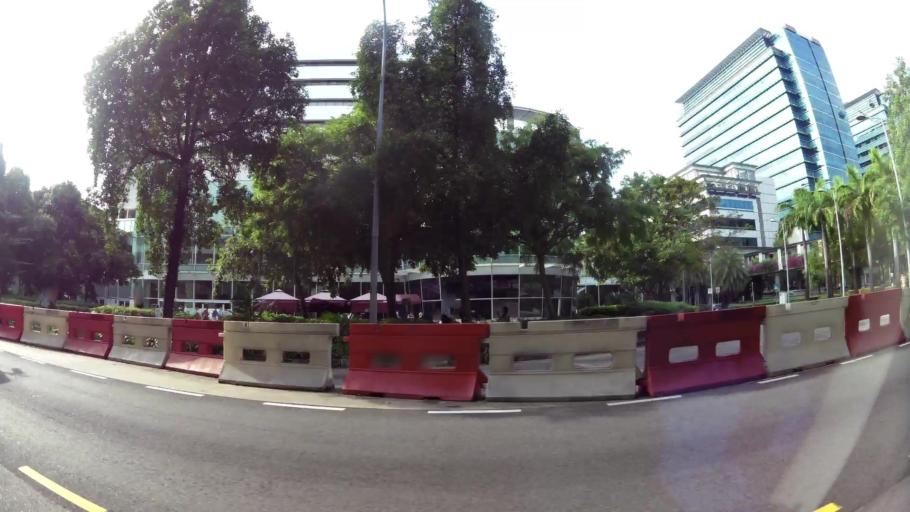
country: SG
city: Singapore
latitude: 1.2653
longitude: 103.8202
